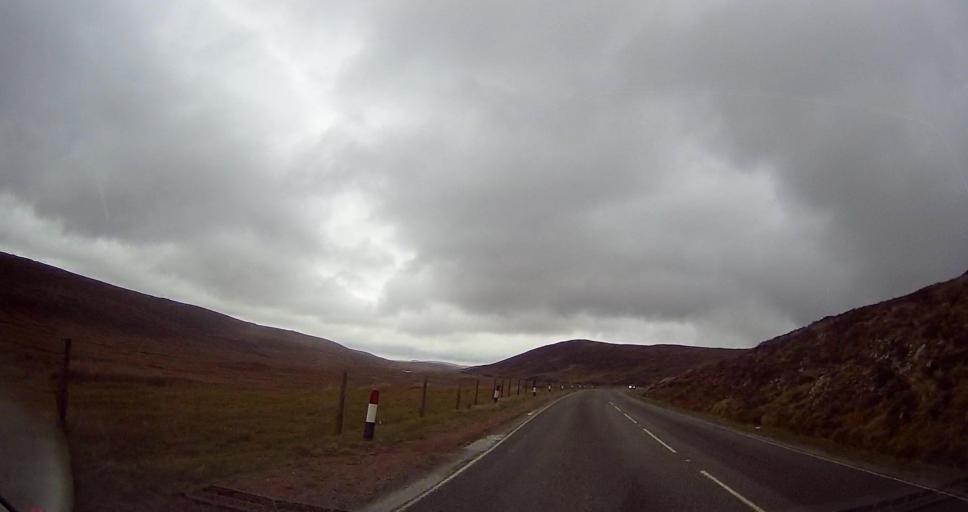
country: GB
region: Scotland
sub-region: Shetland Islands
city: Lerwick
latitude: 60.2956
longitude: -1.2396
